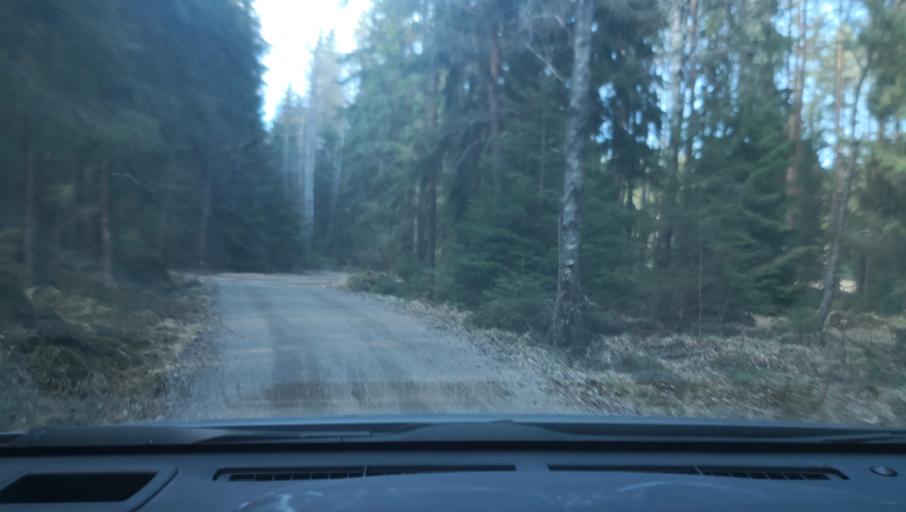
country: SE
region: Uppsala
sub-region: Heby Kommun
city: Heby
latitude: 59.8422
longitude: 16.8472
